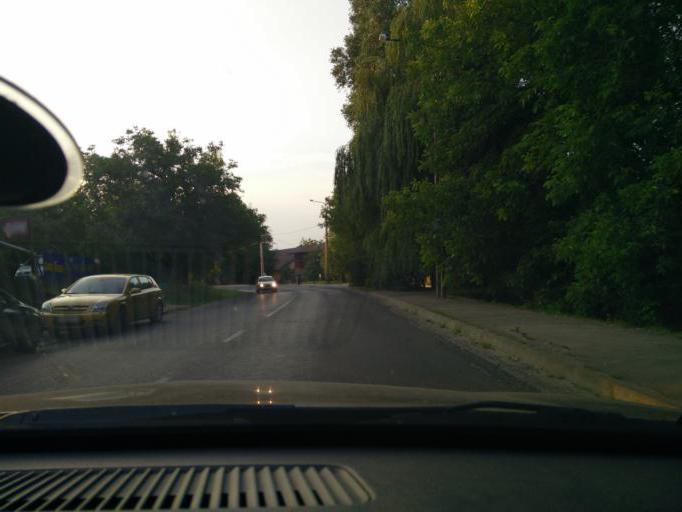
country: HU
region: Pest
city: Toeroekbalint
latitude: 47.4477
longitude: 18.9089
